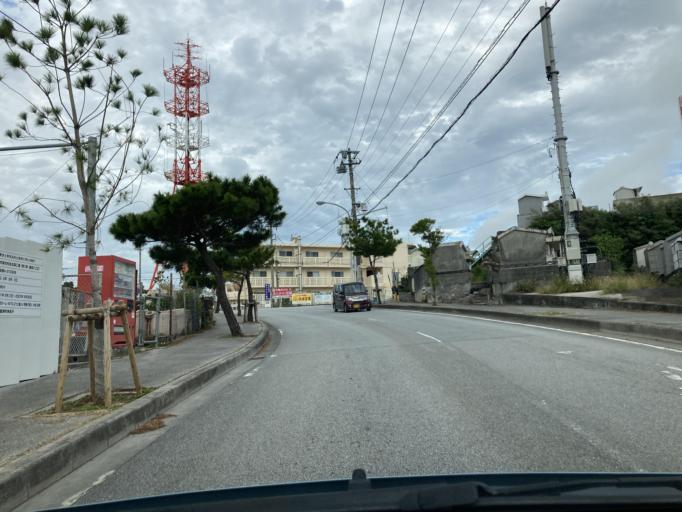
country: JP
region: Okinawa
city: Naha-shi
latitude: 26.2169
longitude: 127.7337
